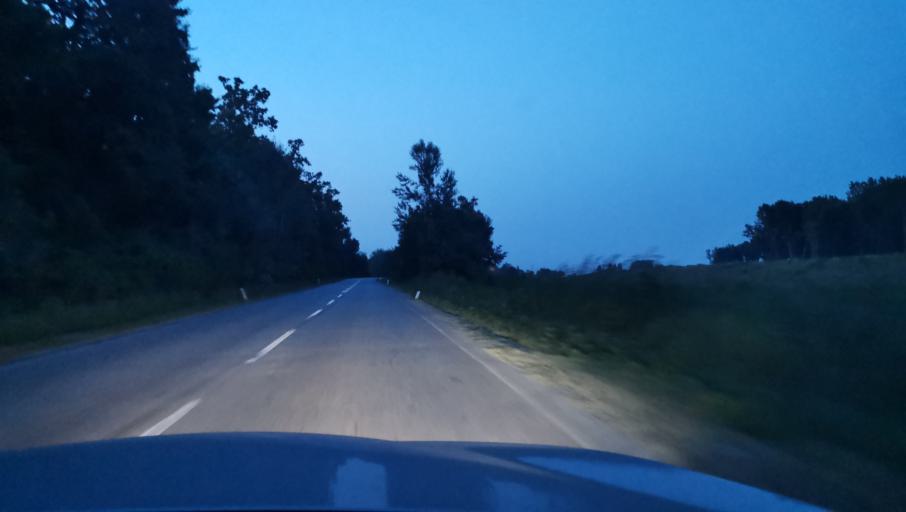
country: RS
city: Boljevci
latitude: 44.7090
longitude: 20.2062
